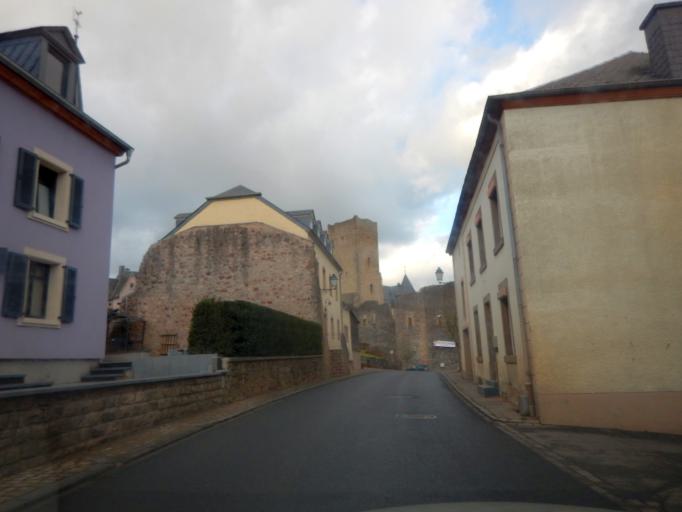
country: LU
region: Diekirch
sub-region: Canton de Redange
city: Useldange
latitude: 49.7671
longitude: 5.9797
